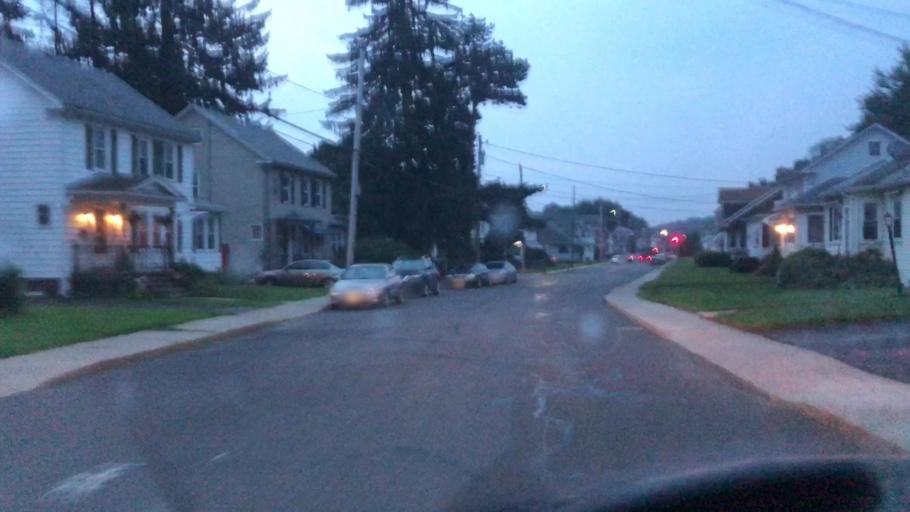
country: US
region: Massachusetts
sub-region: Hampden County
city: Holyoke
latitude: 42.2018
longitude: -72.6340
